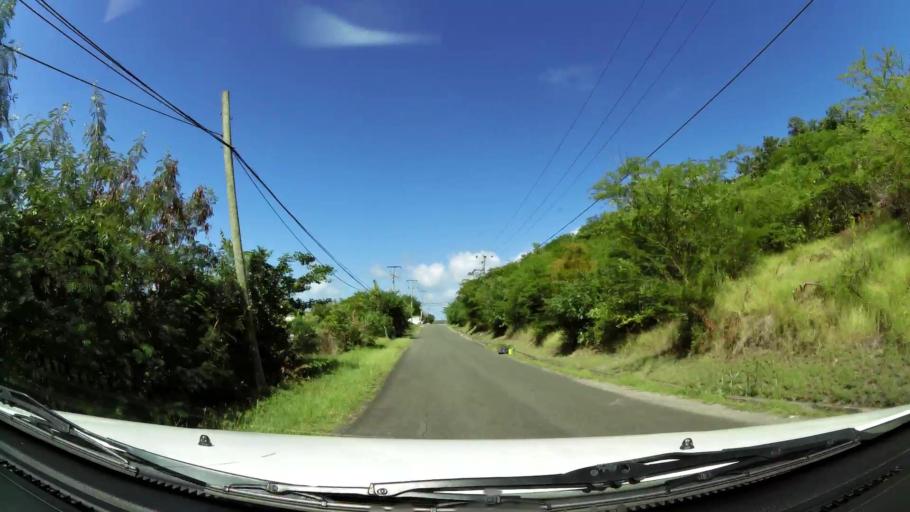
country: LC
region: Vieux-Fort
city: Vieux Fort
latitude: 13.7225
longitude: -60.9506
